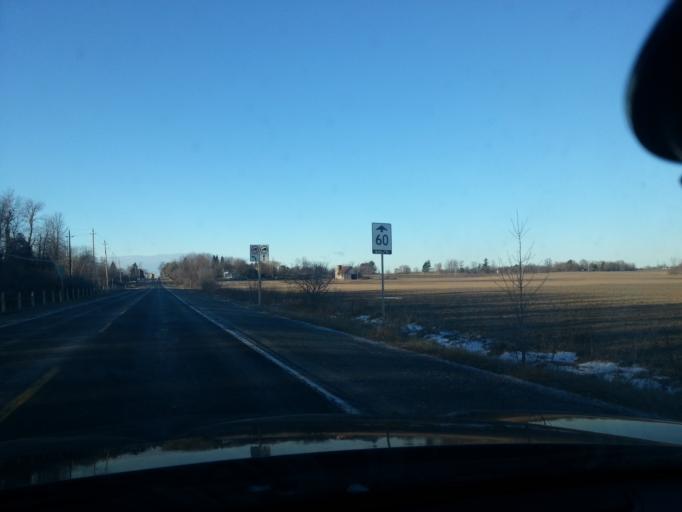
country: CA
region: Ontario
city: Bells Corners
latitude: 45.2207
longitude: -75.7095
